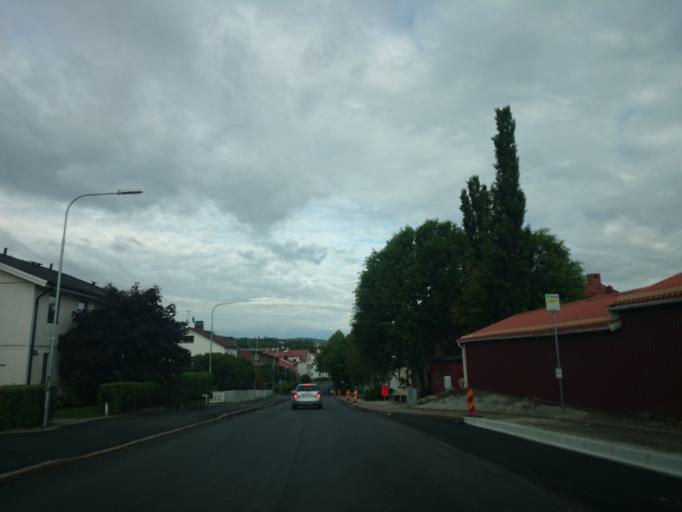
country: SE
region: Vaesternorrland
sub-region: Sundsvalls Kommun
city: Sundsvall
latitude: 62.3808
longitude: 17.3284
